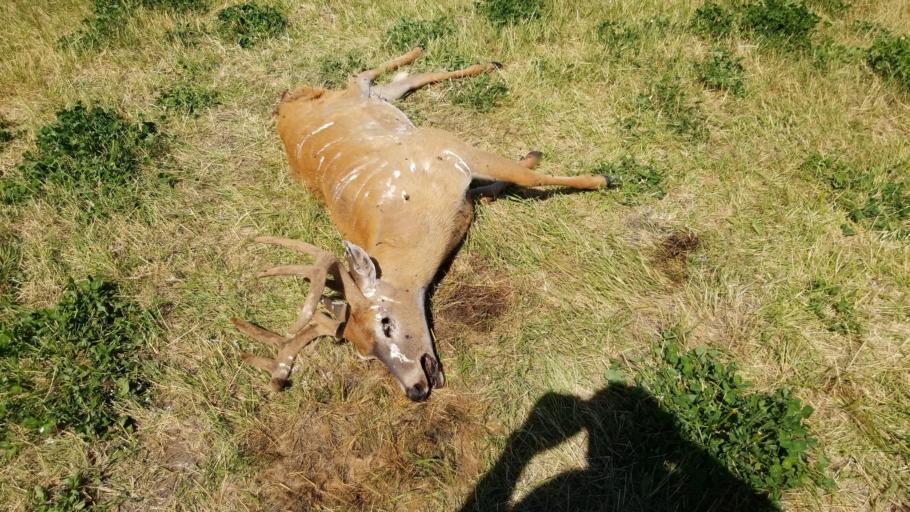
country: US
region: Idaho
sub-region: Lewis County
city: Nezperce
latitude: 46.1623
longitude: -116.1462
